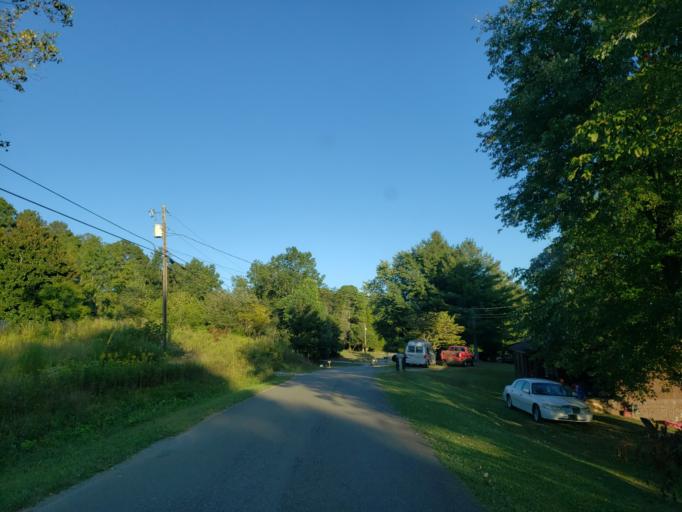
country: US
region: Georgia
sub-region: Pickens County
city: Jasper
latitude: 34.4558
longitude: -84.4468
